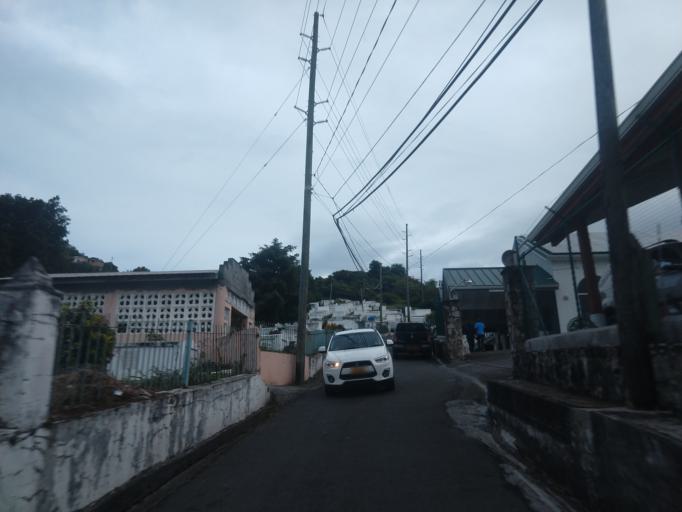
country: GD
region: Saint George
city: Saint George's
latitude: 12.0573
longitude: -61.7539
